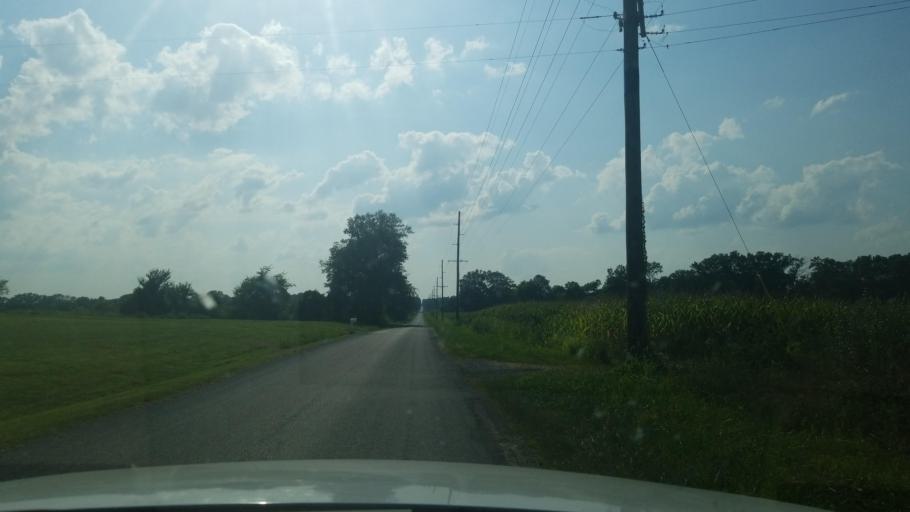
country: US
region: Illinois
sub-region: Saline County
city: Eldorado
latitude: 37.8631
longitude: -88.5125
